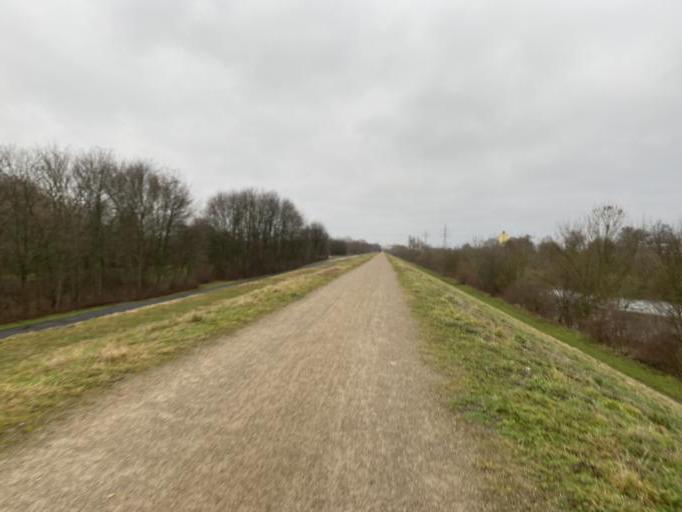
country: DE
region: North Rhine-Westphalia
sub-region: Regierungsbezirk Arnsberg
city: Hamm
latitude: 51.6782
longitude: 7.7615
